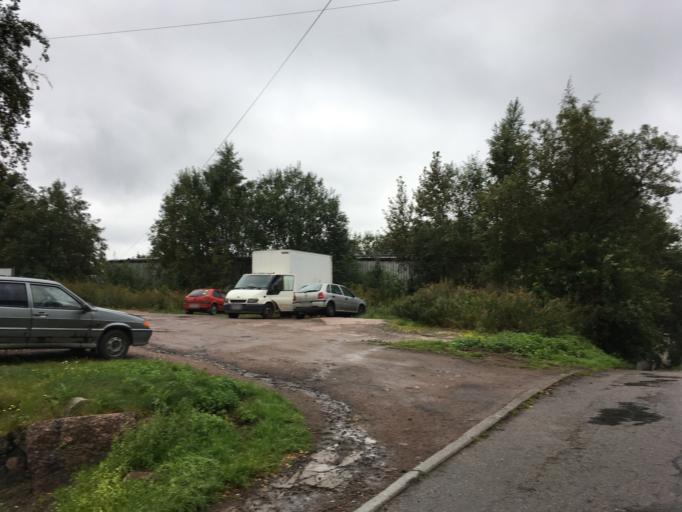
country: RU
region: Leningrad
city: Vyborg
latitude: 60.7117
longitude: 28.7334
